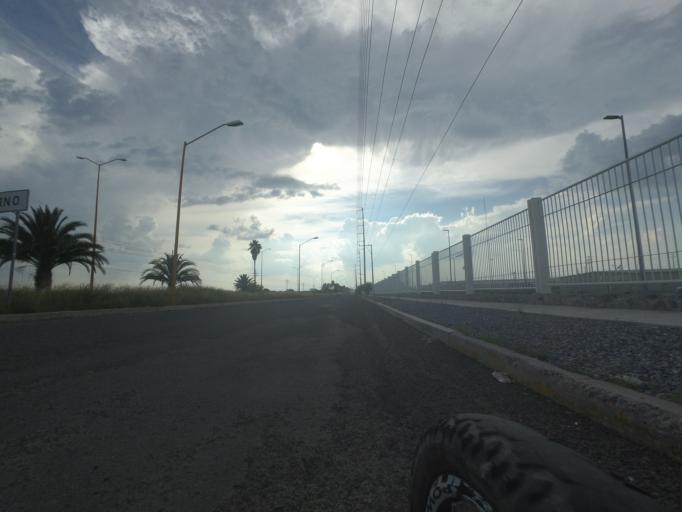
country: MX
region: Aguascalientes
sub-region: Aguascalientes
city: Penuelas (El Cienegal)
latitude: 21.7250
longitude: -102.2929
